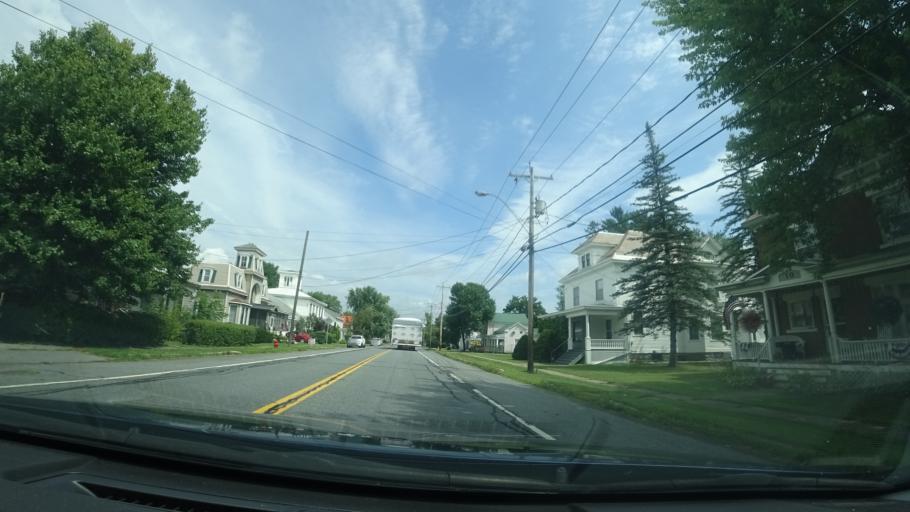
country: US
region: New York
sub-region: Warren County
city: Queensbury
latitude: 43.4103
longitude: -73.4891
